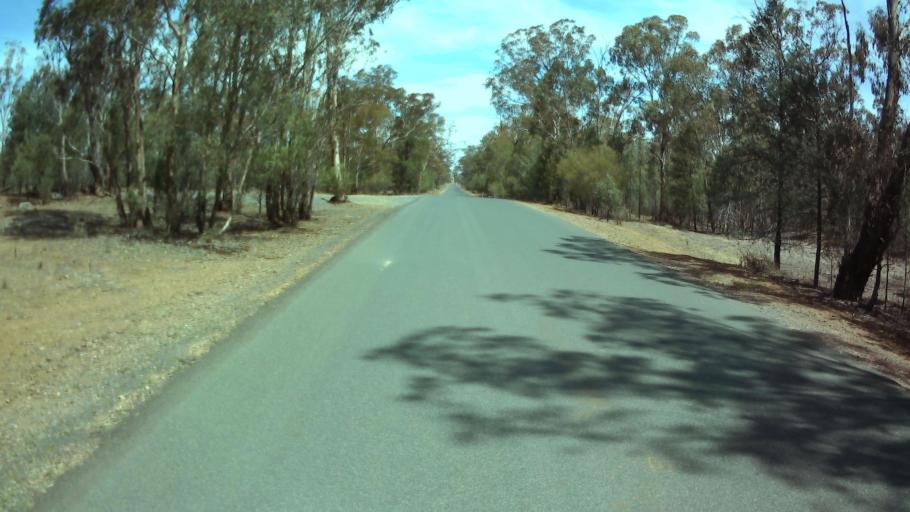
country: AU
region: New South Wales
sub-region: Weddin
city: Grenfell
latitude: -33.8502
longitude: 147.7442
